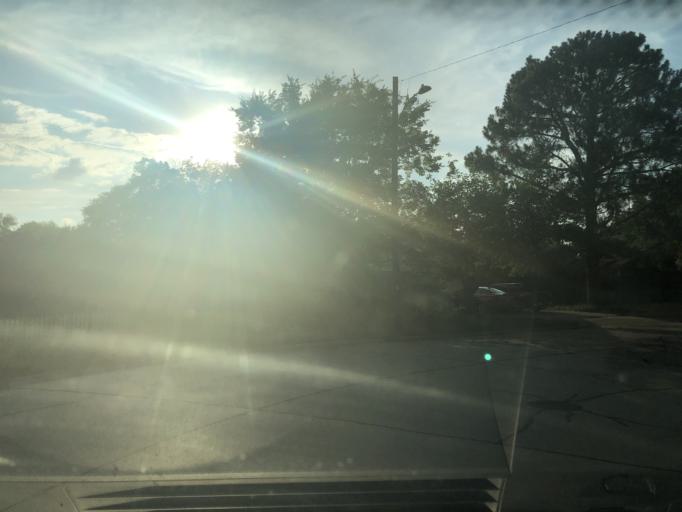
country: US
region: Texas
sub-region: Dallas County
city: Irving
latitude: 32.7912
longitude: -96.9526
